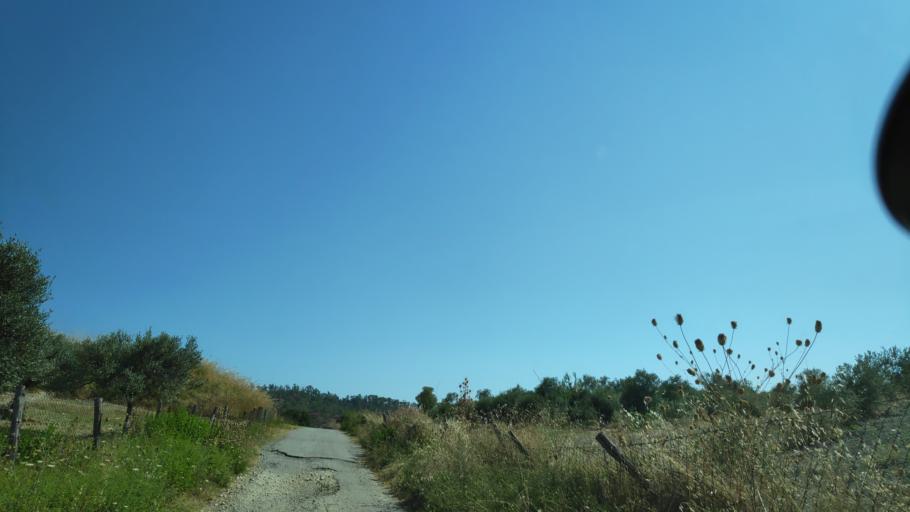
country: IT
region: Calabria
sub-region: Provincia di Reggio Calabria
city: Monasterace
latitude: 38.4327
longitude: 16.5249
